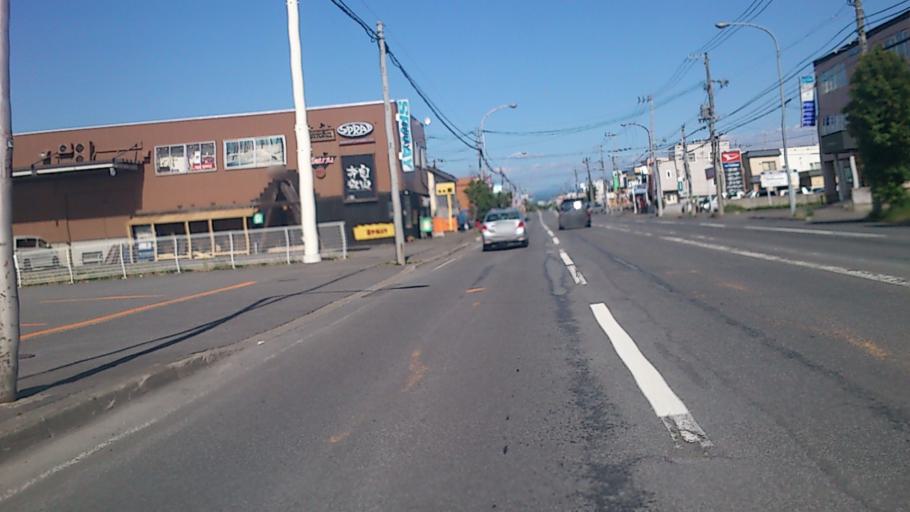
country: JP
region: Hokkaido
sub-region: Asahikawa-shi
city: Asahikawa
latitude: 43.7698
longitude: 142.3895
